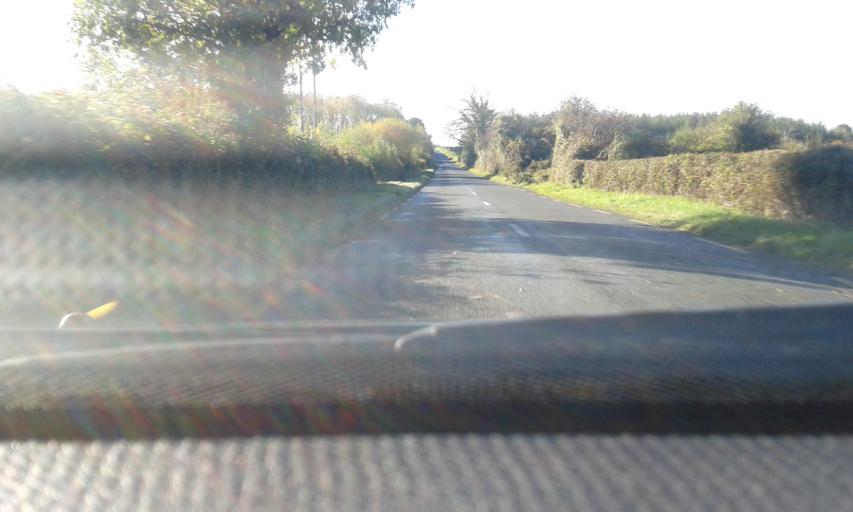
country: IE
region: Leinster
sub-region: Kildare
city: Monasterevin
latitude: 53.1664
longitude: -7.0345
